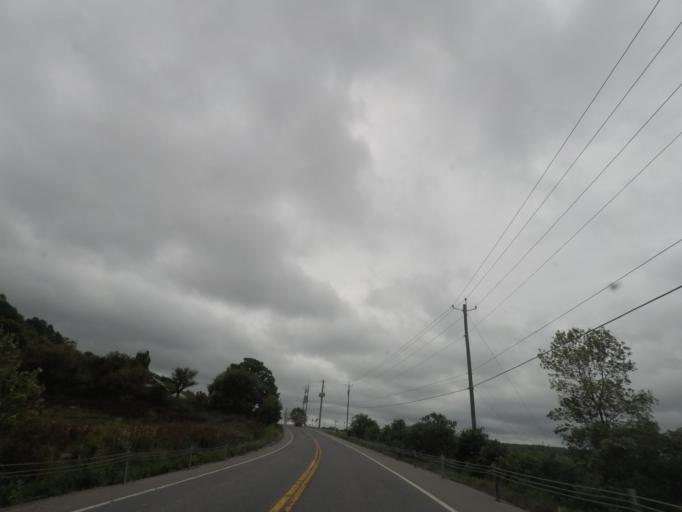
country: US
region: New York
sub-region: Saratoga County
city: Country Knolls
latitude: 42.9286
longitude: -73.7634
